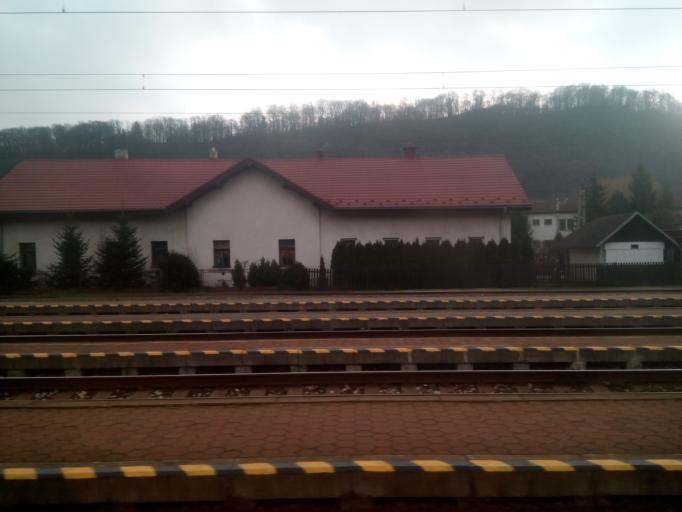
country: SK
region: Kosicky
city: Kosice
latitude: 48.8535
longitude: 21.2241
